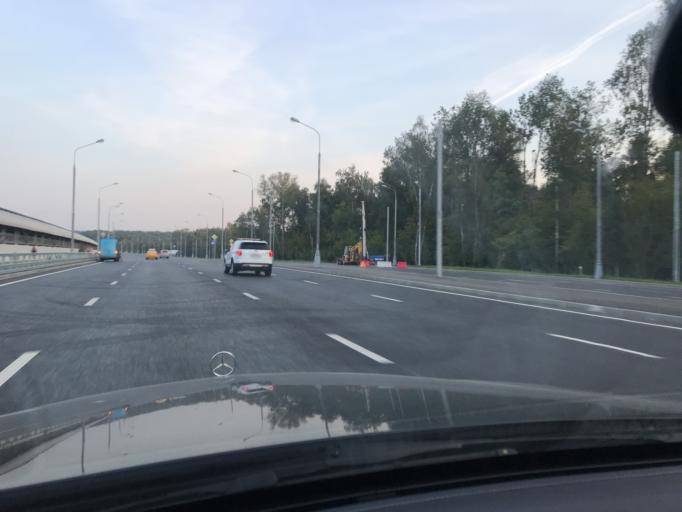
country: RU
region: Moskovskaya
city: Mosrentgen
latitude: 55.5935
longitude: 37.4192
